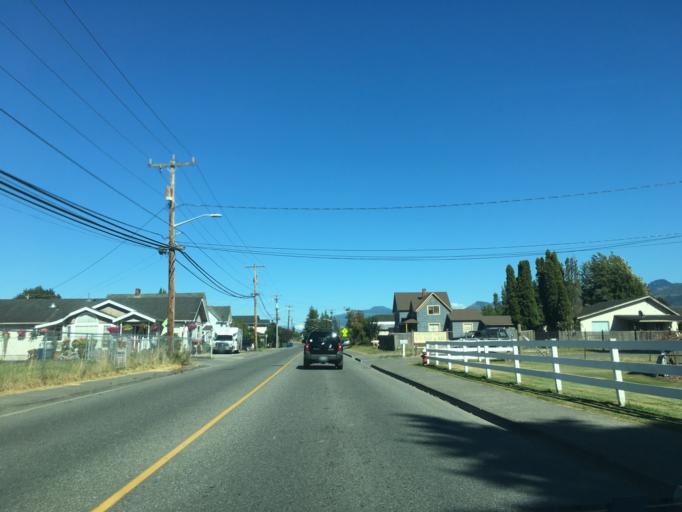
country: US
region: Washington
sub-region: Skagit County
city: Sedro-Woolley
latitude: 48.5030
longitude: -122.2456
